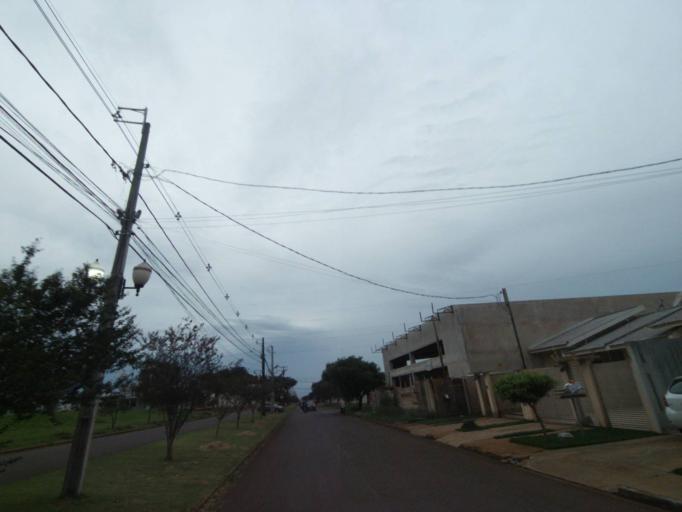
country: BR
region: Parana
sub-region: Campo Mourao
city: Campo Mourao
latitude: -24.0390
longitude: -52.3641
